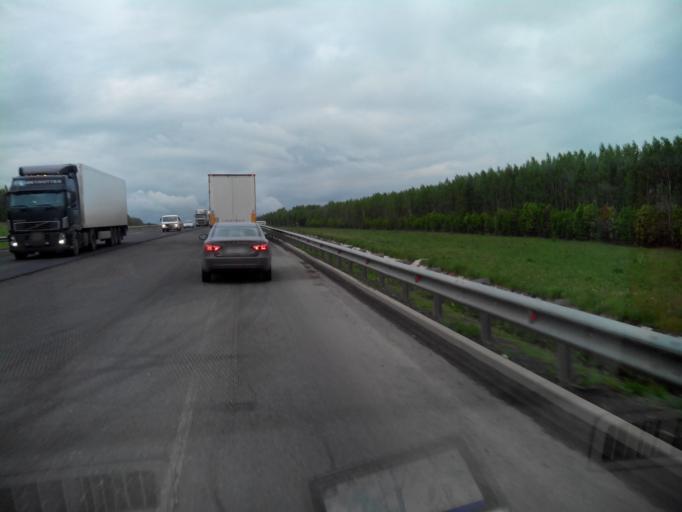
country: RU
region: Penza
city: Gorodishche
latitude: 53.2564
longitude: 45.5183
